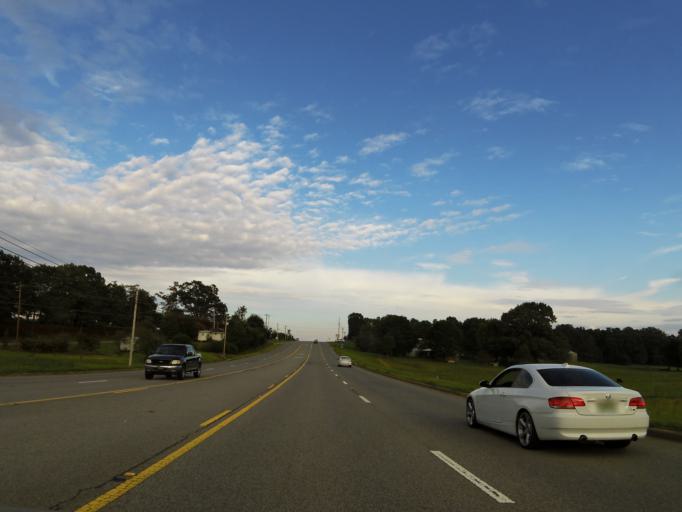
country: US
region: Alabama
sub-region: Lauderdale County
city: Rogersville
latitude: 34.8161
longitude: -87.2632
